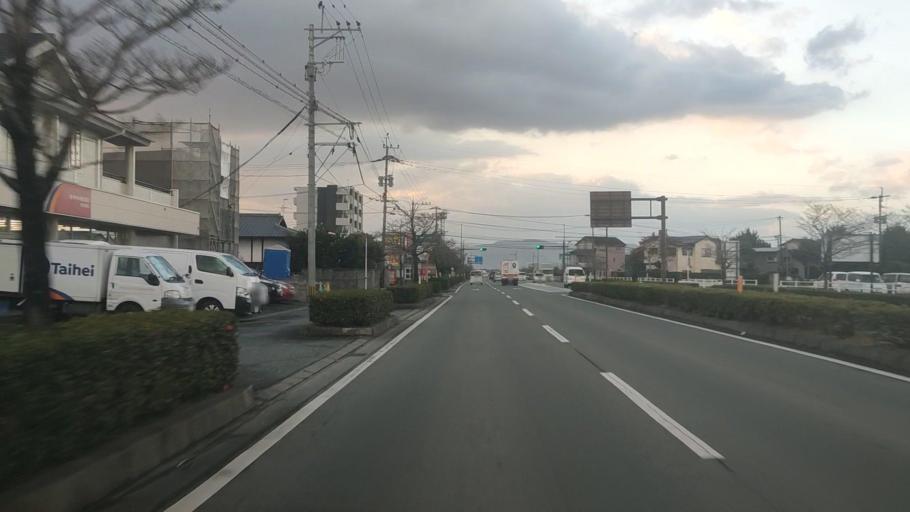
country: JP
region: Kumamoto
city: Kumamoto
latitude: 32.7607
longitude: 130.7057
